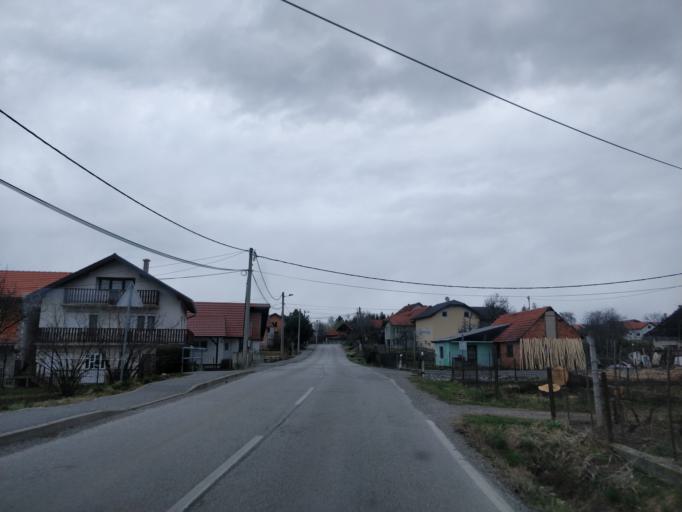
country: HR
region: Zagrebacka
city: Jakovlje
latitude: 45.9163
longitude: 15.8914
